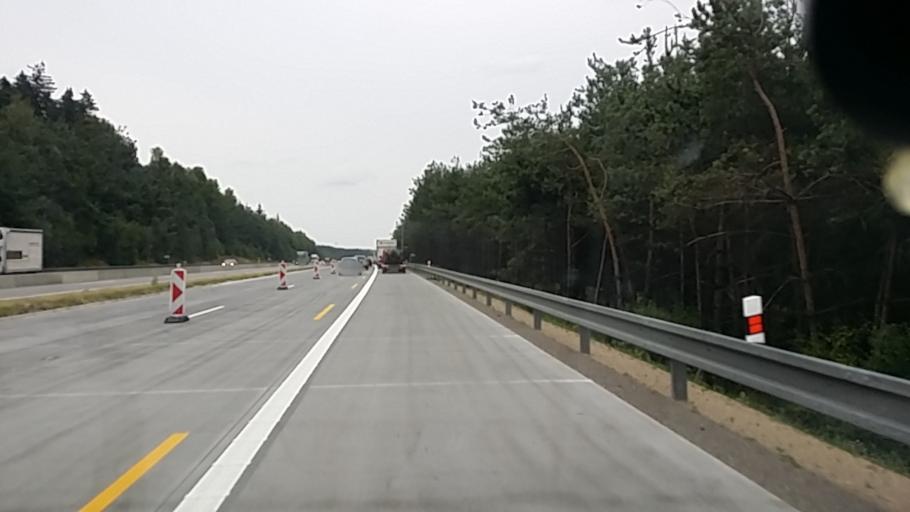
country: CZ
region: Vysocina
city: Velky Beranov
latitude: 49.4244
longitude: 15.6749
